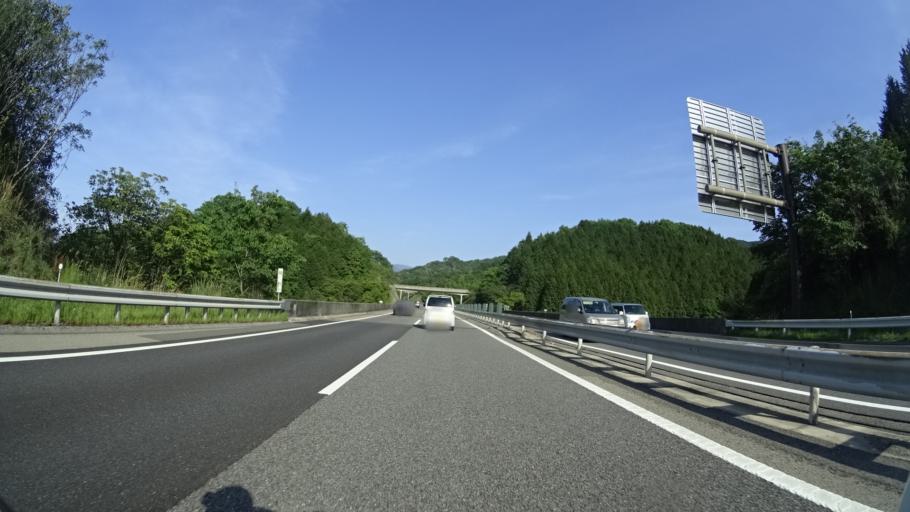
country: JP
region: Ehime
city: Saijo
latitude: 33.8834
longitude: 133.1147
